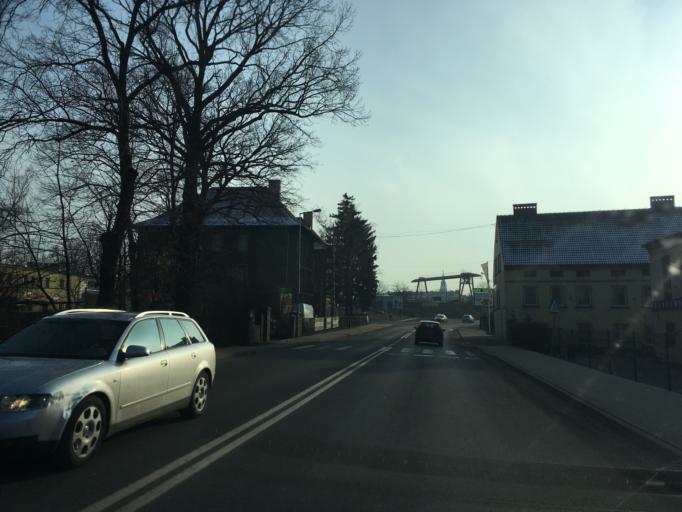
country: PL
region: Lower Silesian Voivodeship
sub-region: Powiat boleslawiecki
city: Boleslawiec
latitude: 51.2688
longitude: 15.5675
